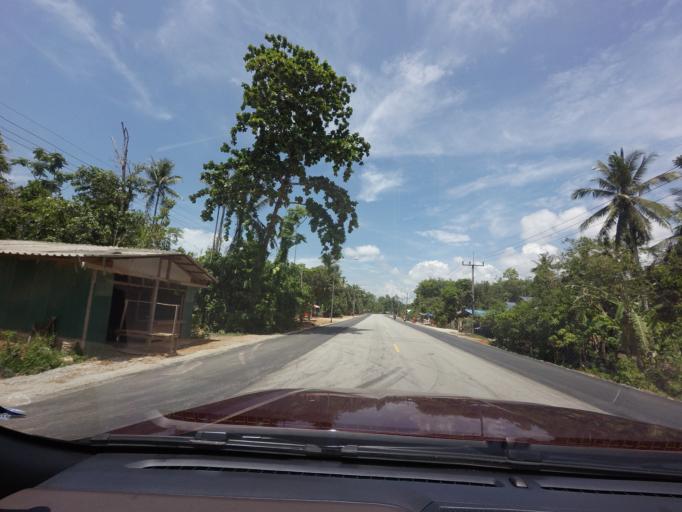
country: TH
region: Narathiwat
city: Ra-ngae
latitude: 6.2776
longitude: 101.6996
